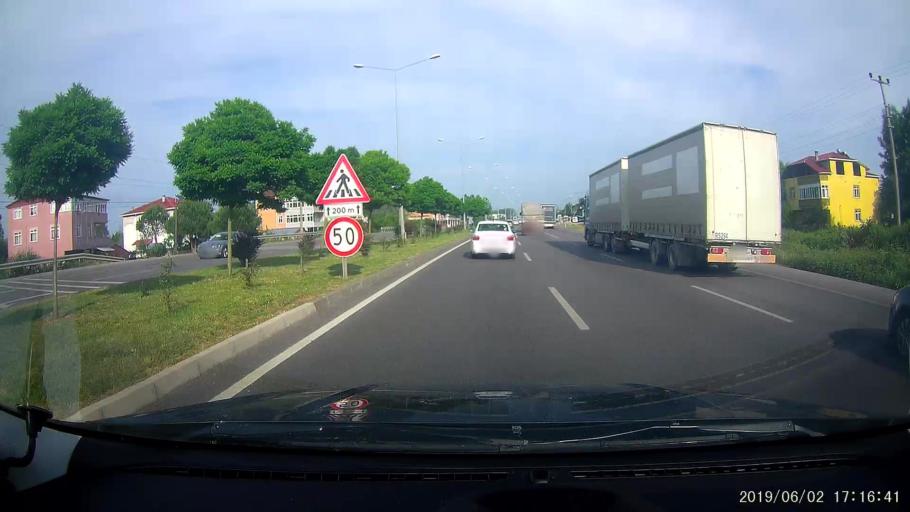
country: TR
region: Samsun
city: Dikbiyik
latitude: 41.2333
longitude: 36.5702
